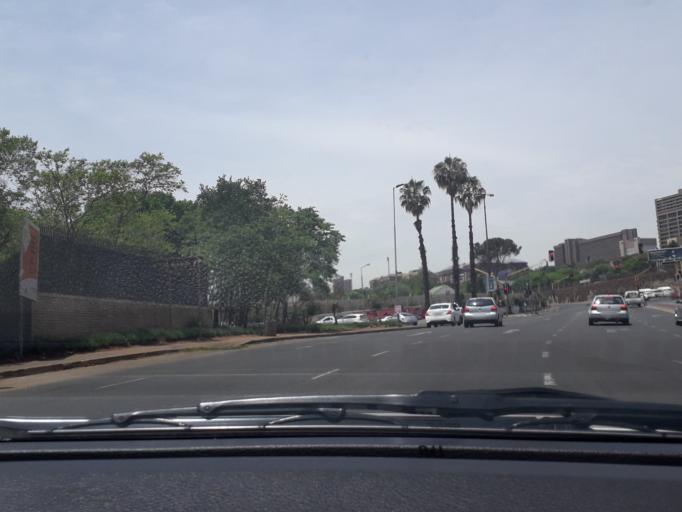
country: ZA
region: Gauteng
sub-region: City of Johannesburg Metropolitan Municipality
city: Johannesburg
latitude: -26.1861
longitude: 28.0314
